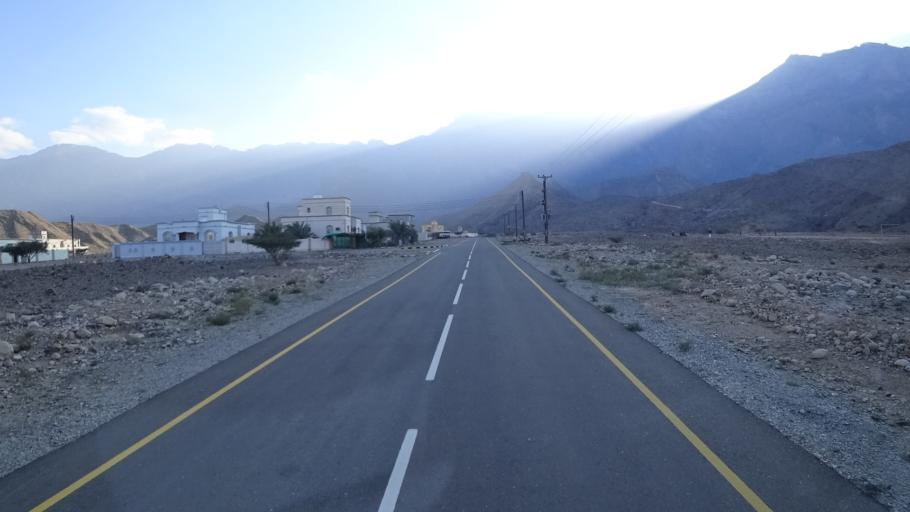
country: OM
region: Al Batinah
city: Rustaq
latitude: 23.2681
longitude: 57.3235
